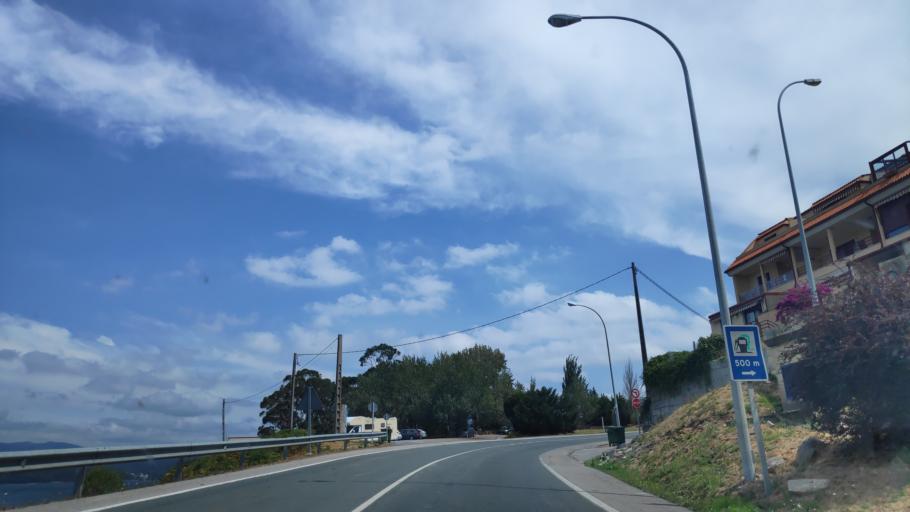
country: ES
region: Galicia
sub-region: Provincia de Pontevedra
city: Vilagarcia de Arousa
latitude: 42.6199
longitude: -8.7742
